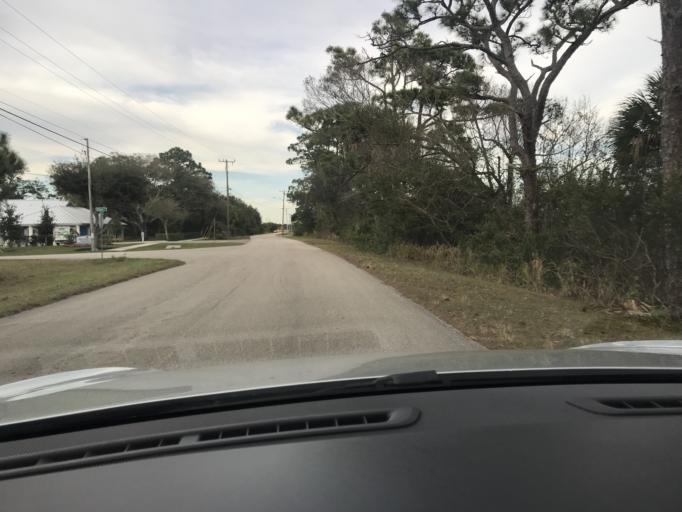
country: US
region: Florida
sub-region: Saint Lucie County
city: Lakewood Park
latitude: 27.4904
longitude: -80.3741
